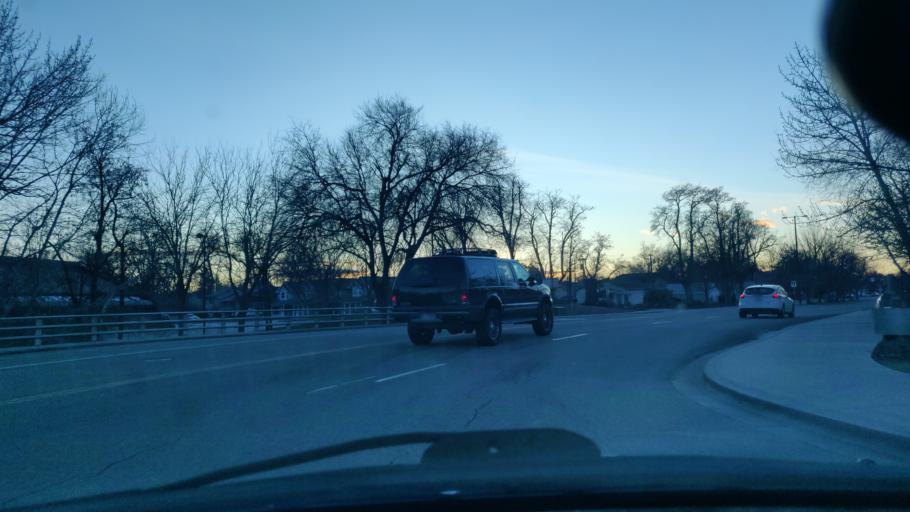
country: US
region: Idaho
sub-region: Ada County
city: Boise
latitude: 43.5987
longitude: -116.1875
